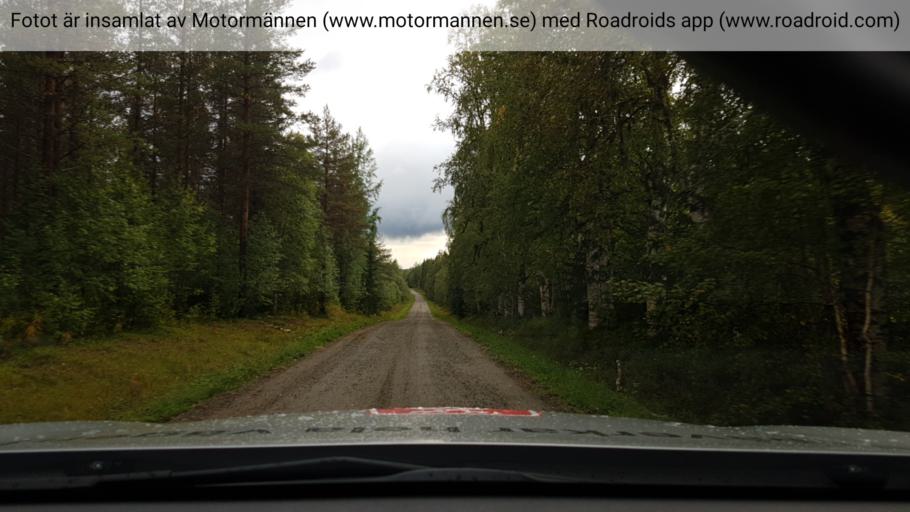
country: SE
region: Vaesterbotten
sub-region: Asele Kommun
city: Asele
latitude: 64.1441
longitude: 16.9006
